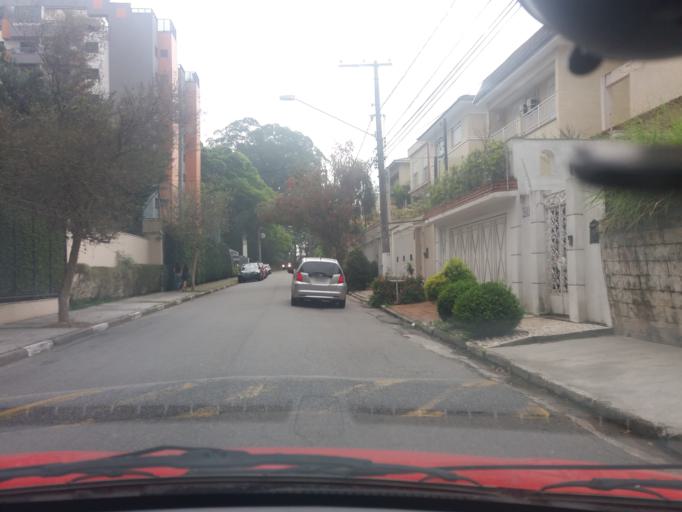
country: BR
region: Sao Paulo
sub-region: Taboao Da Serra
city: Taboao da Serra
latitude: -23.5993
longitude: -46.7254
